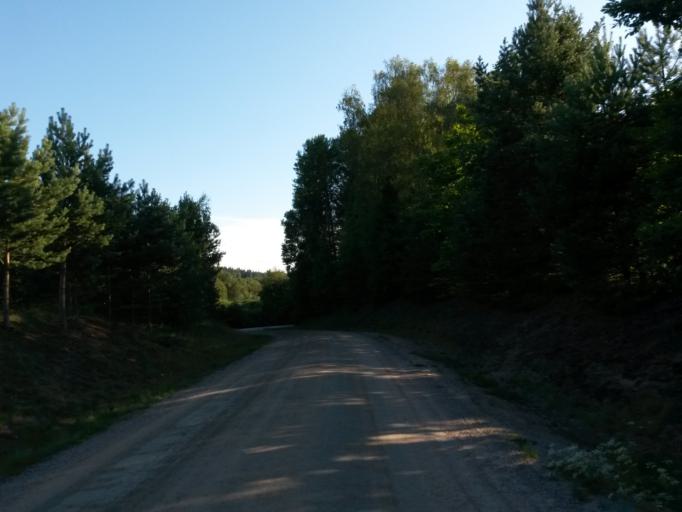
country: SE
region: Vaestra Goetaland
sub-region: Vargarda Kommun
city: Vargarda
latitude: 58.0343
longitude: 12.8477
